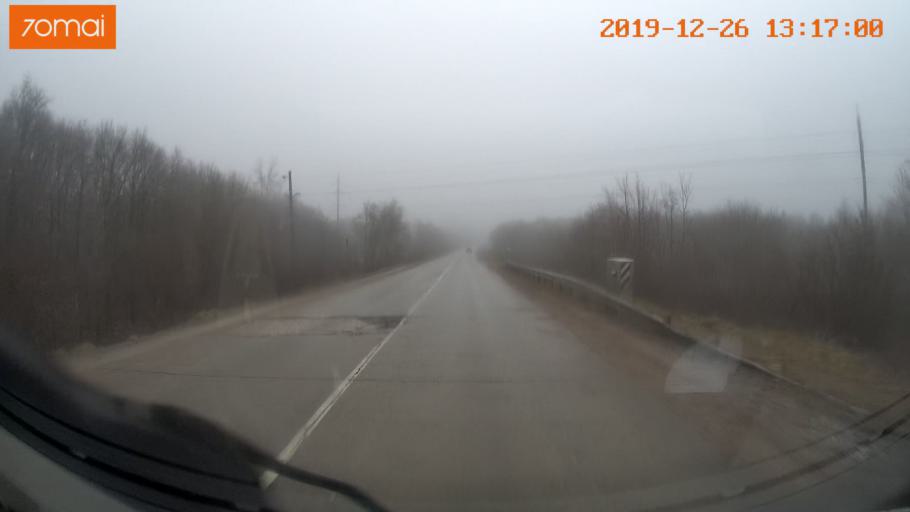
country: RU
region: Vologda
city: Cherepovets
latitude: 58.9750
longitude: 38.1113
